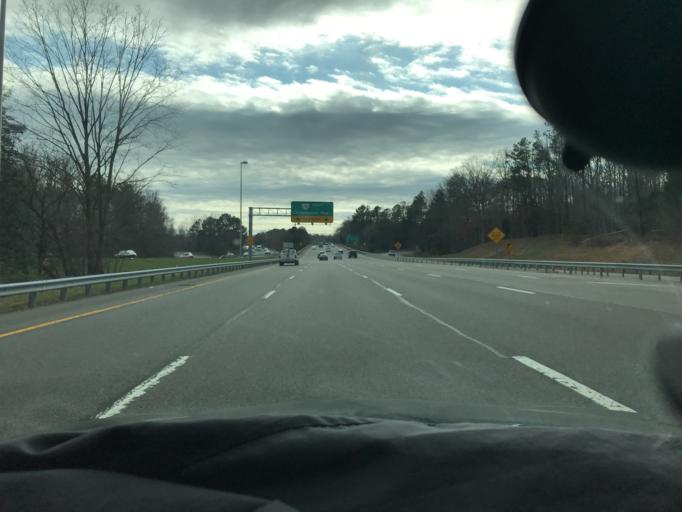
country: US
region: Virginia
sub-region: Chesterfield County
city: Bon Air
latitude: 37.5288
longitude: -77.5241
